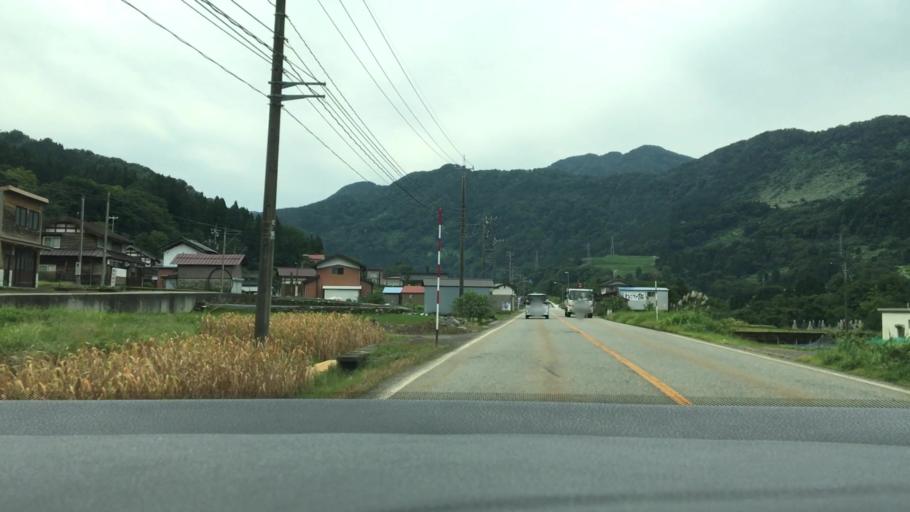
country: JP
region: Ishikawa
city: Tsurugi-asahimachi
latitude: 36.3125
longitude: 136.6468
